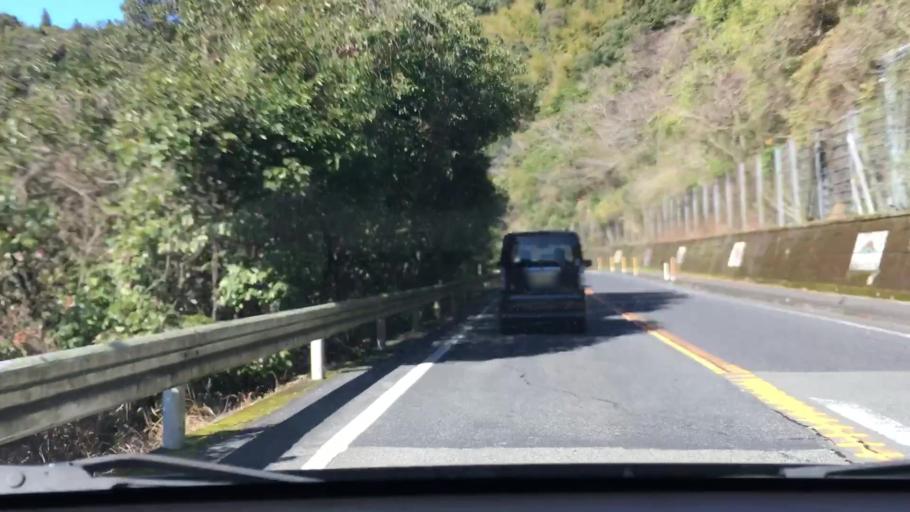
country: JP
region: Kagoshima
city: Kagoshima-shi
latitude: 31.6526
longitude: 130.5075
